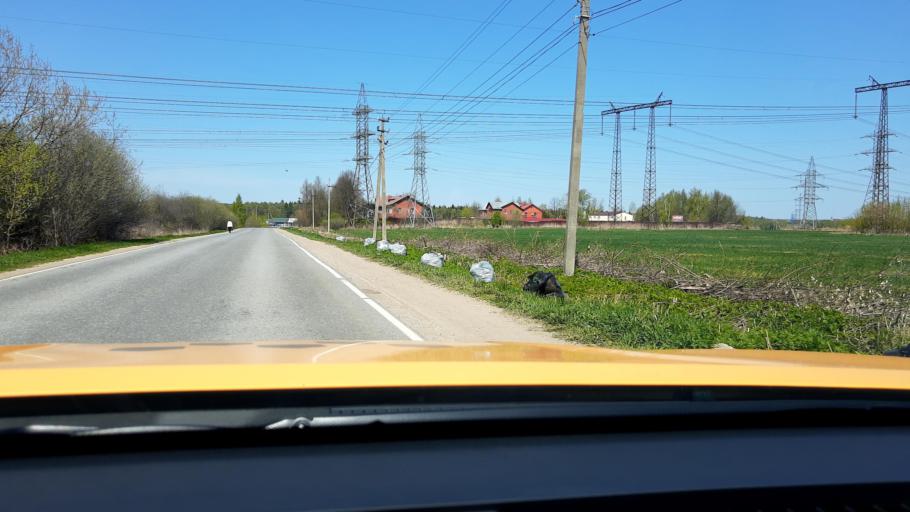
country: RU
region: Moskovskaya
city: Gorki-Leninskiye
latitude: 55.4757
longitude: 37.8377
